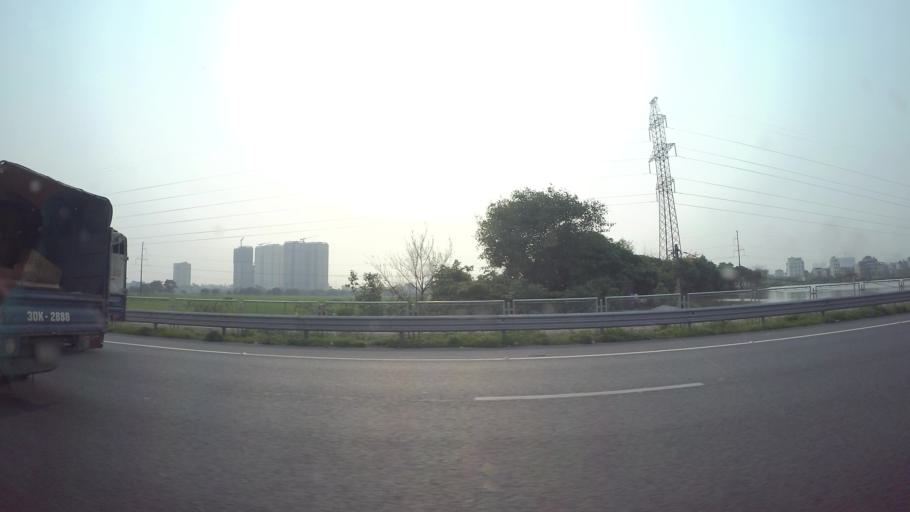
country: VN
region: Ha Noi
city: Van Dien
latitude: 20.9357
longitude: 105.8590
